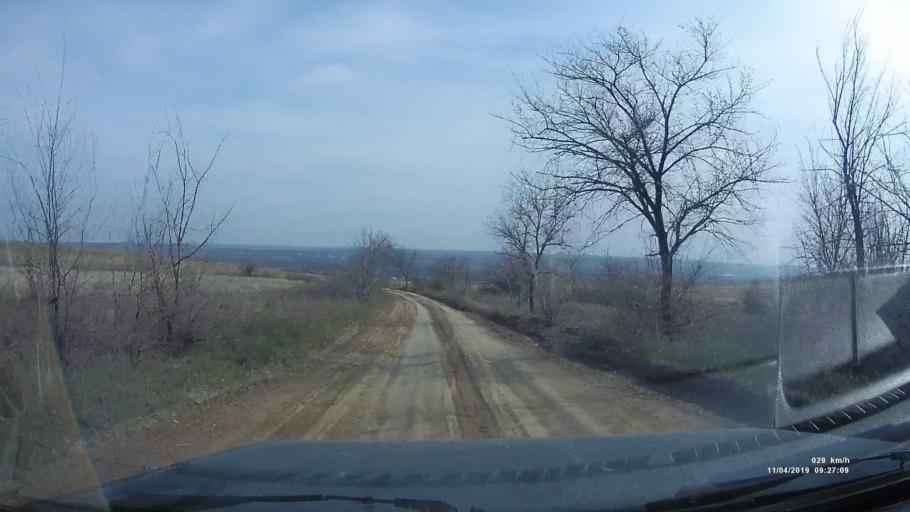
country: RU
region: Rostov
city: Staraya Stanitsa
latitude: 48.2652
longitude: 40.3658
